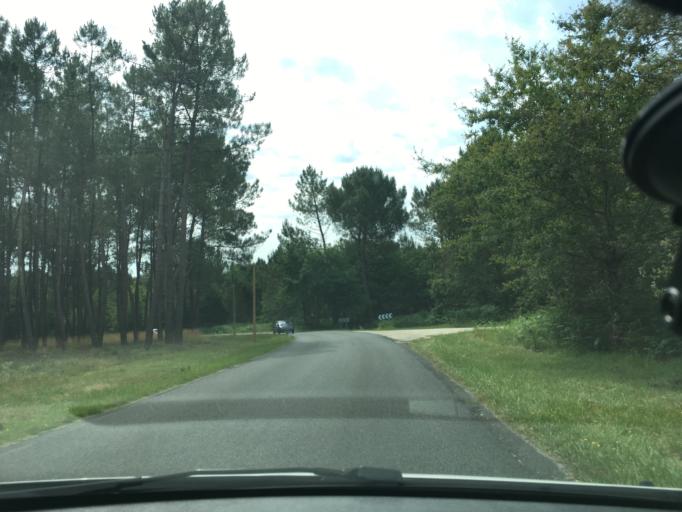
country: FR
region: Aquitaine
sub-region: Departement de la Gironde
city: Gaillan-en-Medoc
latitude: 45.3360
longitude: -1.0033
